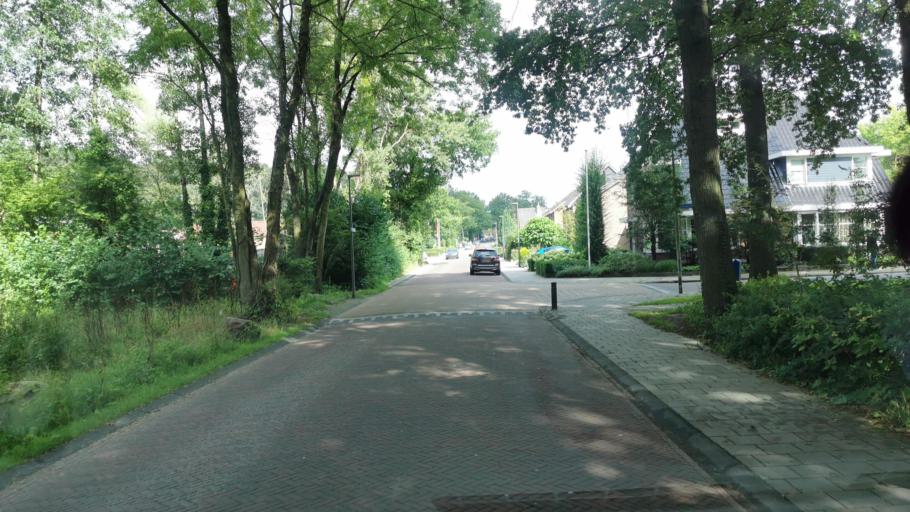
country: NL
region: Overijssel
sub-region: Gemeente Losser
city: Losser
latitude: 52.3115
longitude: 6.9890
